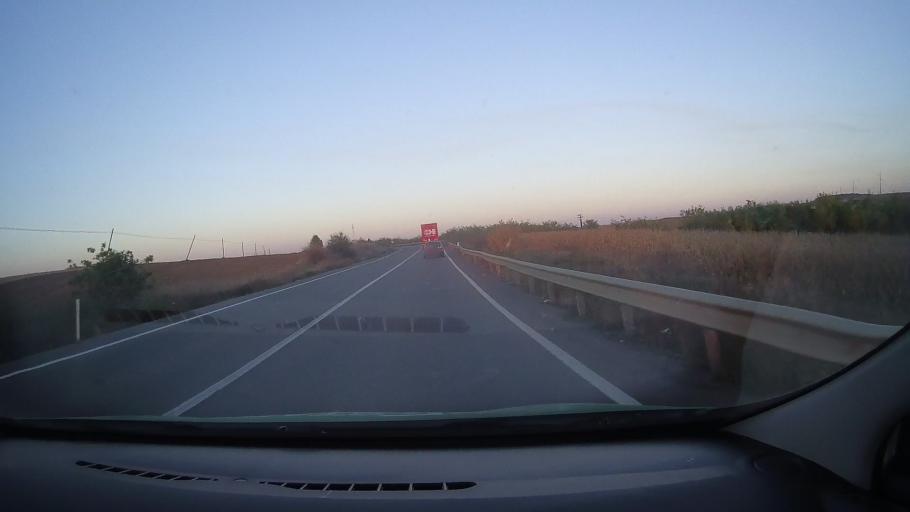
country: RO
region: Bihor
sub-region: Comuna Cherechiu
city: Cherechiu
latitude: 47.3689
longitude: 22.1267
